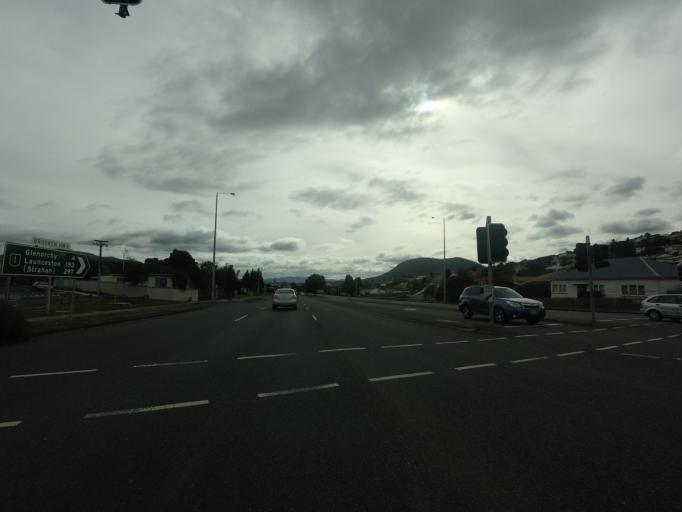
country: AU
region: Tasmania
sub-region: Glenorchy
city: Moonah
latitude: -42.8436
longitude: 147.3070
